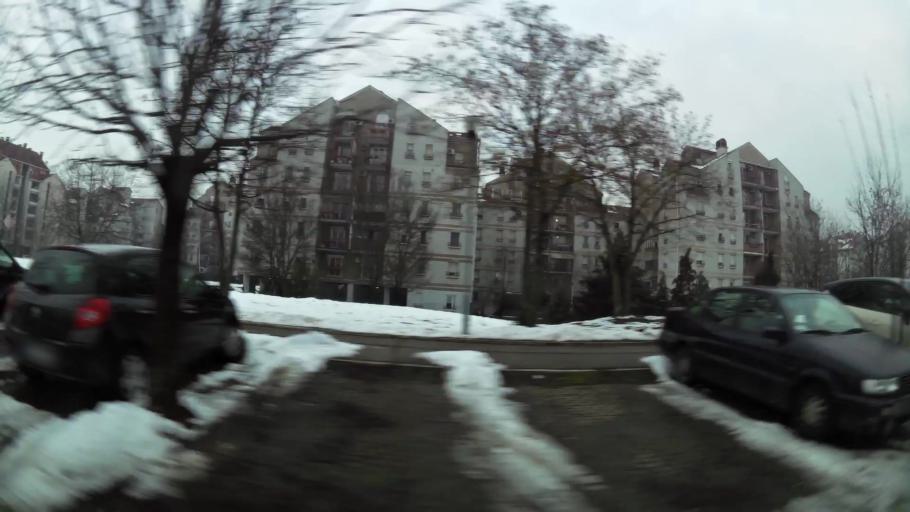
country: RS
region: Central Serbia
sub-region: Belgrade
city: Zemun
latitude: 44.8161
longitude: 20.3809
